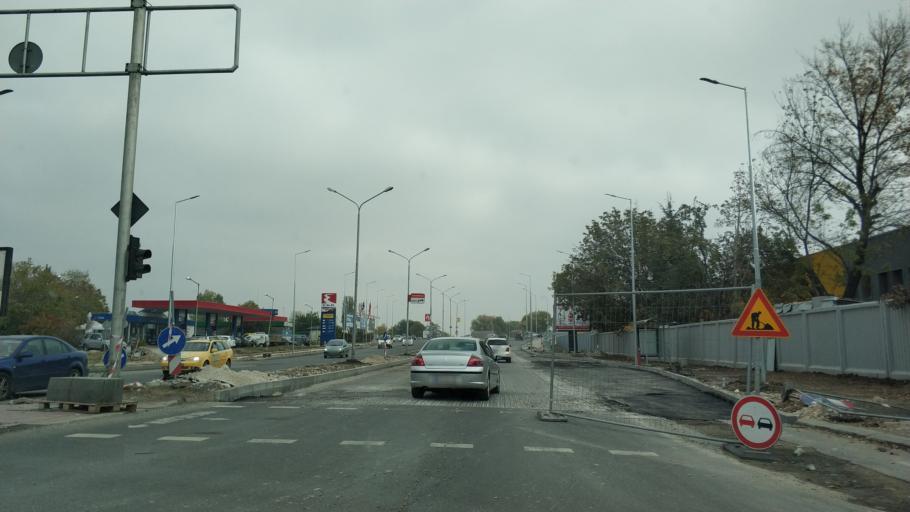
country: BG
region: Plovdiv
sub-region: Obshtina Plovdiv
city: Plovdiv
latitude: 42.1599
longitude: 24.7621
